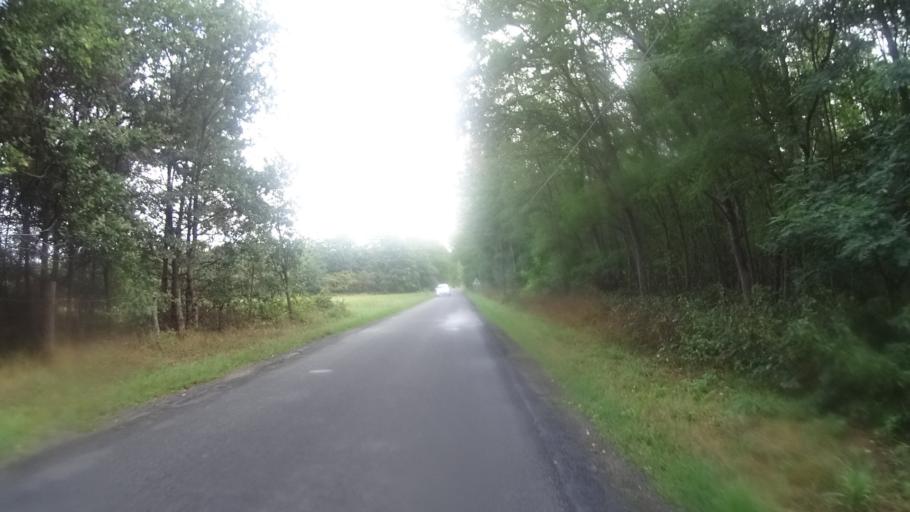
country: FR
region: Centre
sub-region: Departement du Loiret
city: Fay-aux-Loges
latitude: 47.9399
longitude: 2.1584
